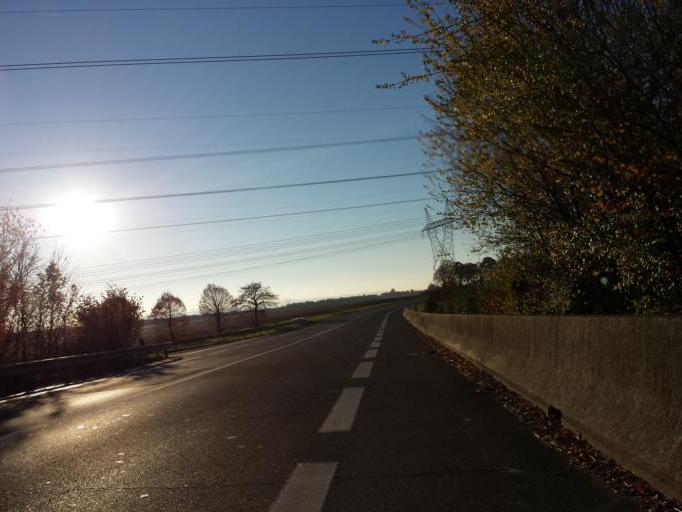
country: FR
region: Ile-de-France
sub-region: Departement du Val-d'Oise
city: Belloy-en-France
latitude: 49.0711
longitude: 2.4050
